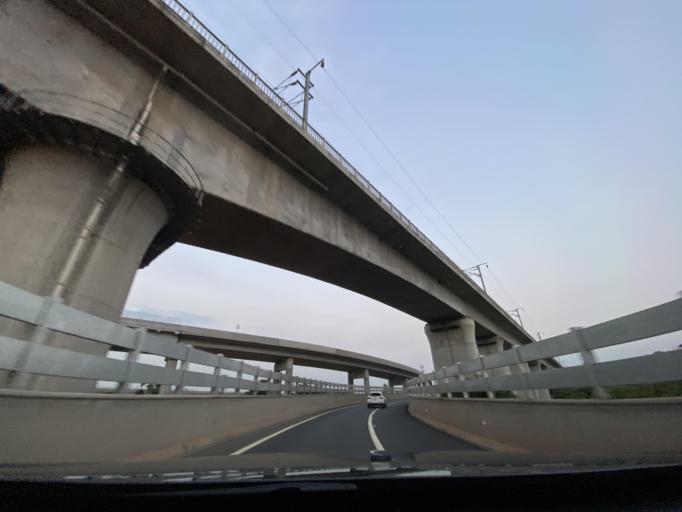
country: CN
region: Sichuan
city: Chengdu
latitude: 30.5717
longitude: 104.1357
